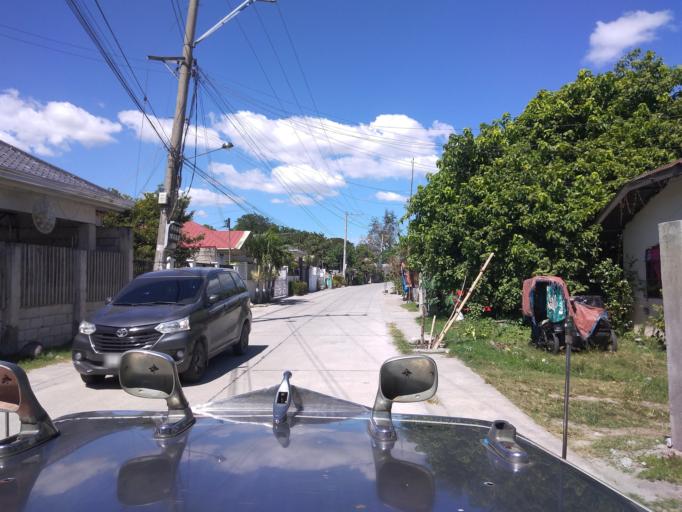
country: PH
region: Central Luzon
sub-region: Province of Pampanga
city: Magliman
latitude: 15.0356
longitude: 120.6469
